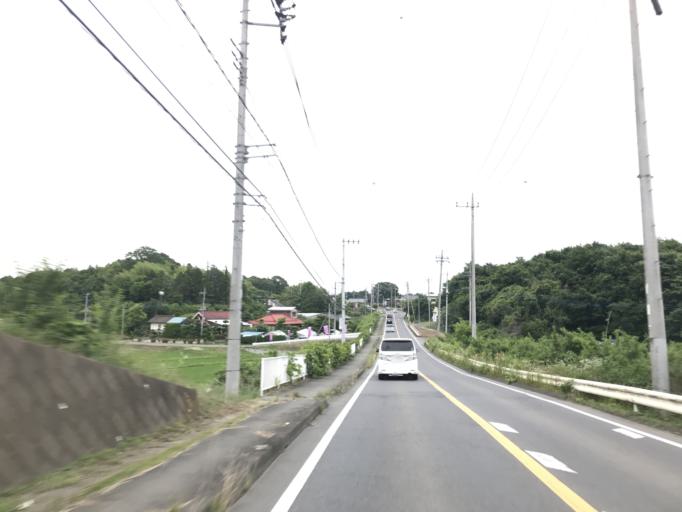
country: JP
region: Ibaraki
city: Ishioka
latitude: 36.2255
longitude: 140.3070
